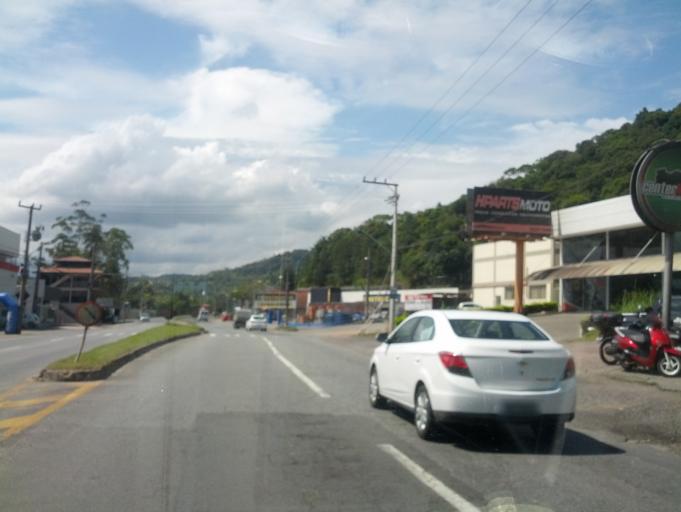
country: BR
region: Santa Catarina
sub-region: Blumenau
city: Blumenau
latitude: -26.9026
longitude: -49.0629
